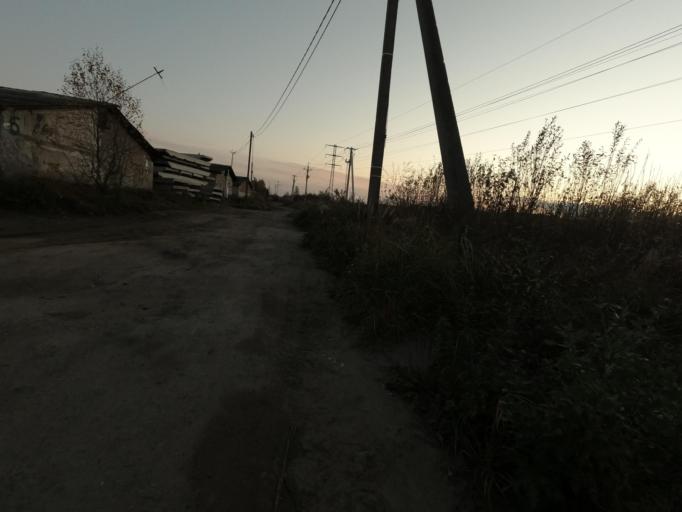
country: RU
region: Leningrad
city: Kirovsk
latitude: 59.8741
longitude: 31.0031
